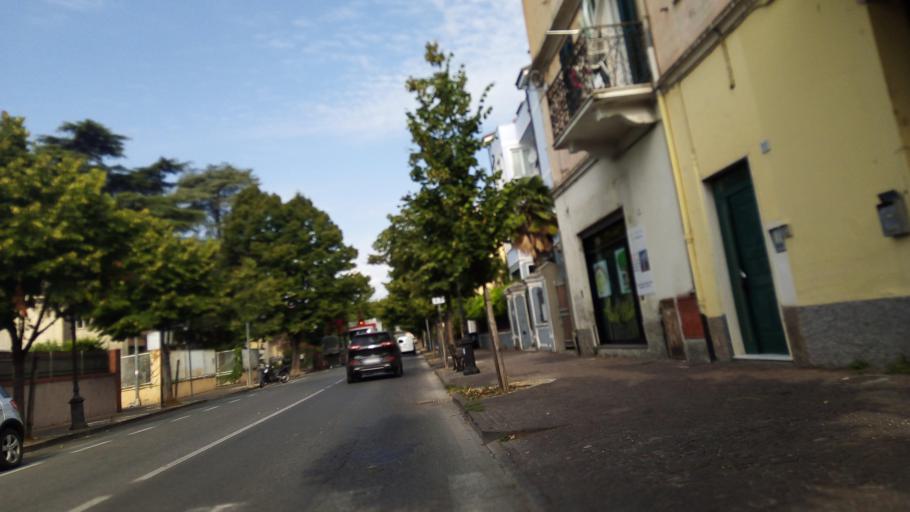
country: IT
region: Liguria
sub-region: Provincia di Savona
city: Albenga
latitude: 44.0508
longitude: 8.2107
